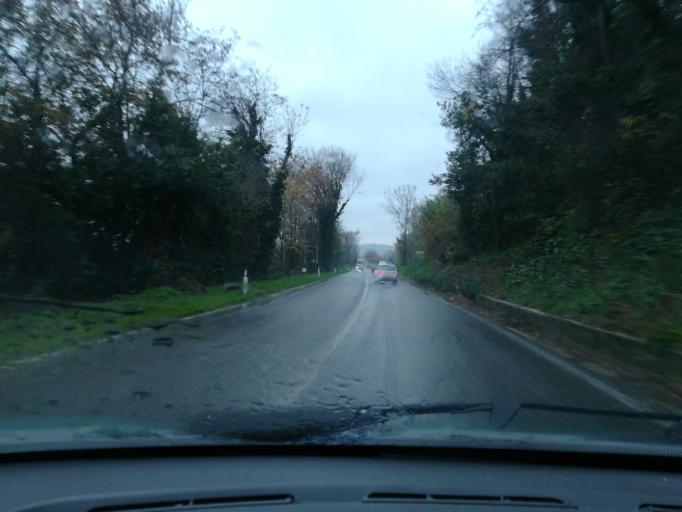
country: IT
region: The Marches
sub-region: Provincia di Macerata
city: Sforzacosta
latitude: 43.2777
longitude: 13.4309
